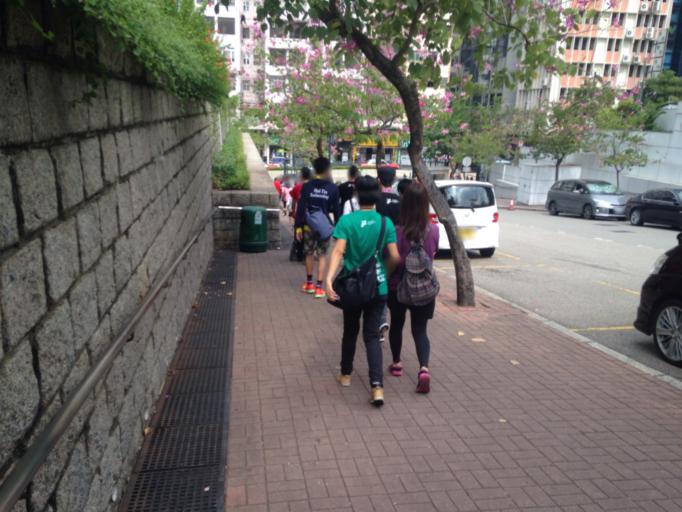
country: HK
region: Kowloon City
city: Kowloon
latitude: 22.3025
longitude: 114.1706
